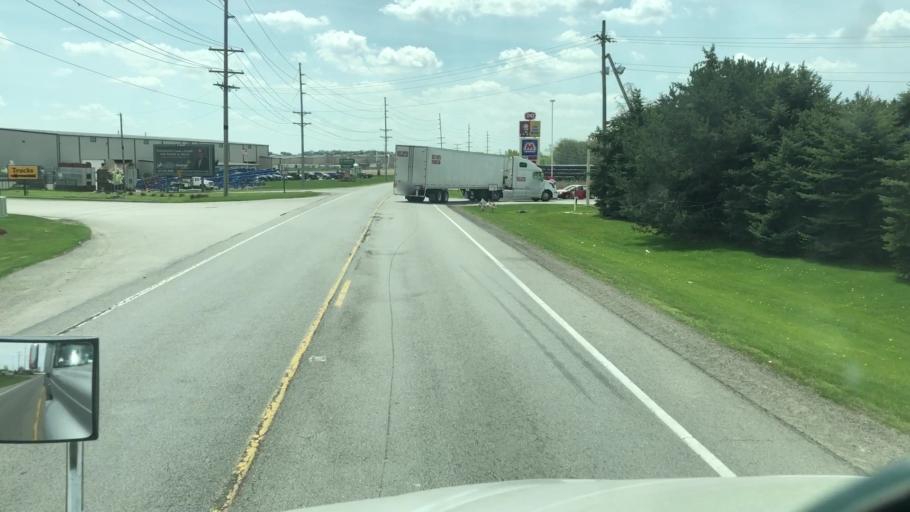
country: US
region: Ohio
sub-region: Wyandot County
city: Upper Sandusky
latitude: 40.8550
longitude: -83.3007
